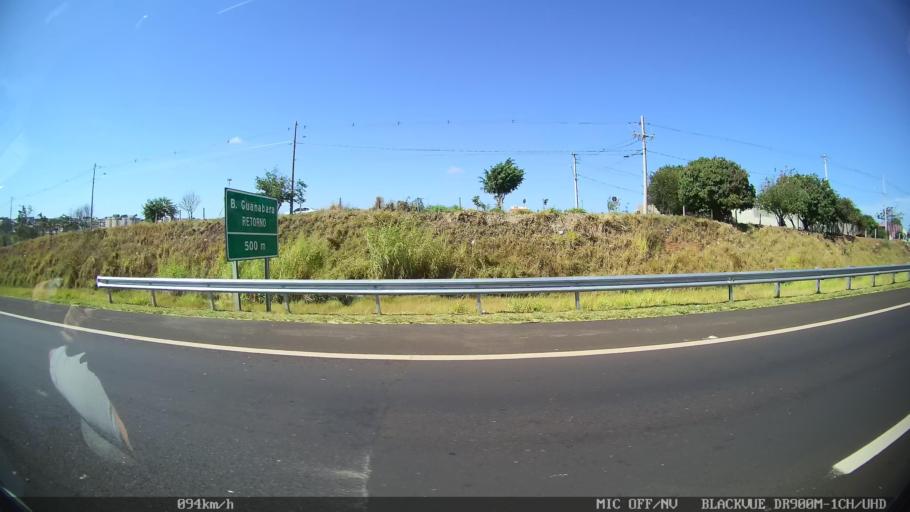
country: BR
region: Sao Paulo
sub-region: Franca
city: Franca
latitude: -20.5232
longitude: -47.4197
